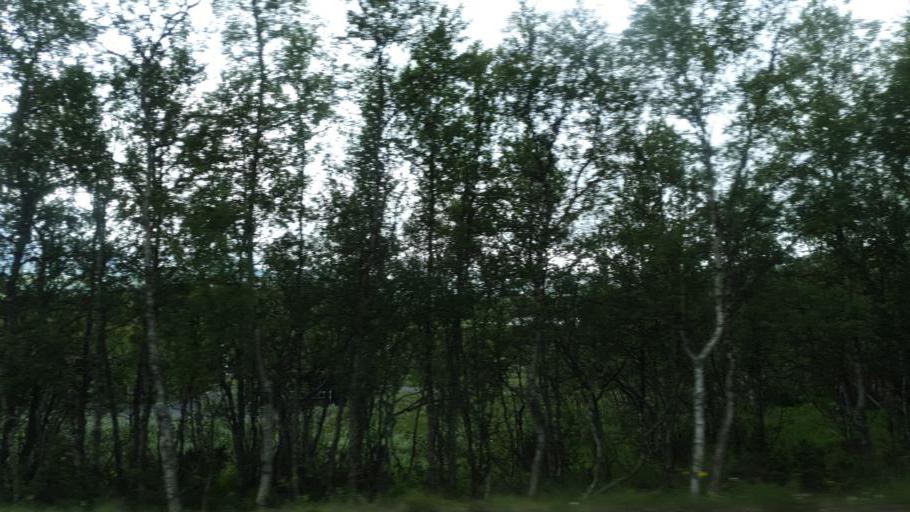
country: NO
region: Oppland
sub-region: Vestre Slidre
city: Slidre
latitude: 61.2583
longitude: 8.8748
